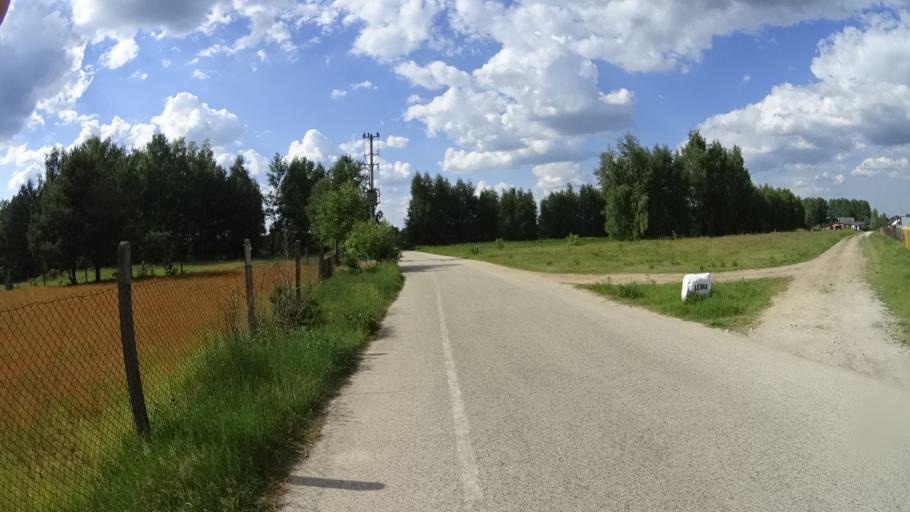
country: PL
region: Masovian Voivodeship
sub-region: Powiat piaseczynski
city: Tarczyn
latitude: 52.0010
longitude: 20.8334
